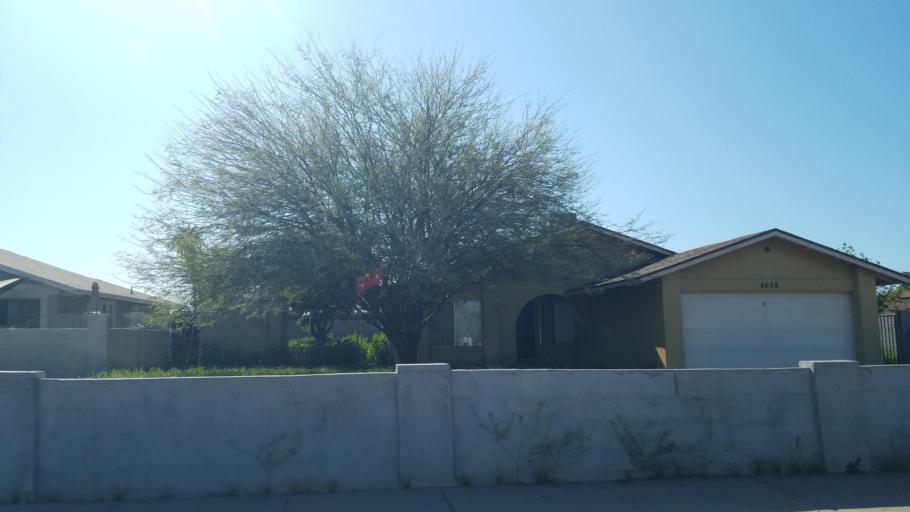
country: US
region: Arizona
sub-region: Maricopa County
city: Glendale
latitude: 33.5636
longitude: -112.1777
